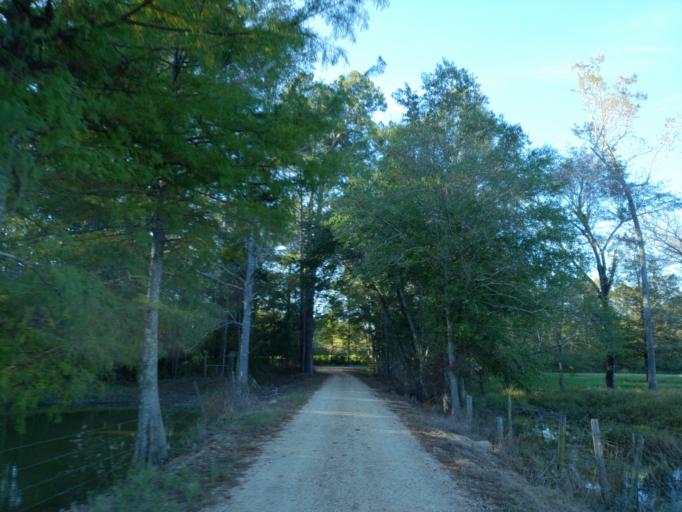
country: US
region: Mississippi
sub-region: Perry County
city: Richton
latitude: 31.3686
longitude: -88.8123
